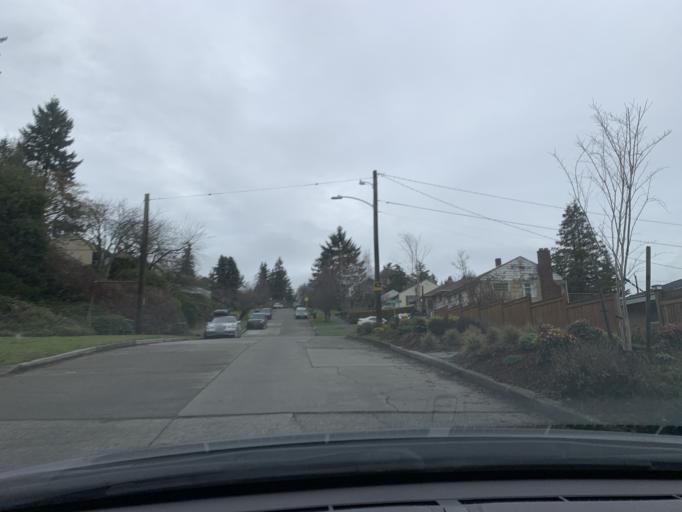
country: US
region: Washington
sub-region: King County
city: White Center
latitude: 47.5627
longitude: -122.3962
